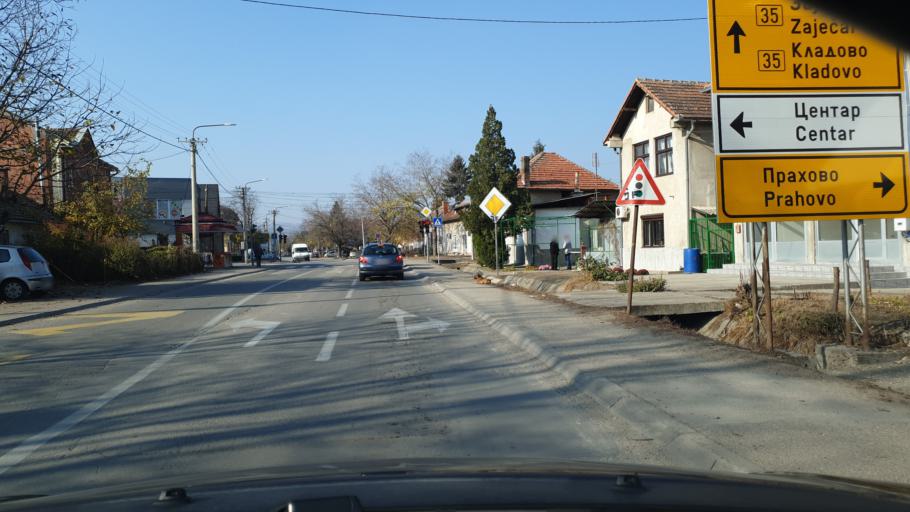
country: RS
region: Central Serbia
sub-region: Borski Okrug
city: Negotin
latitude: 44.2316
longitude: 22.5342
